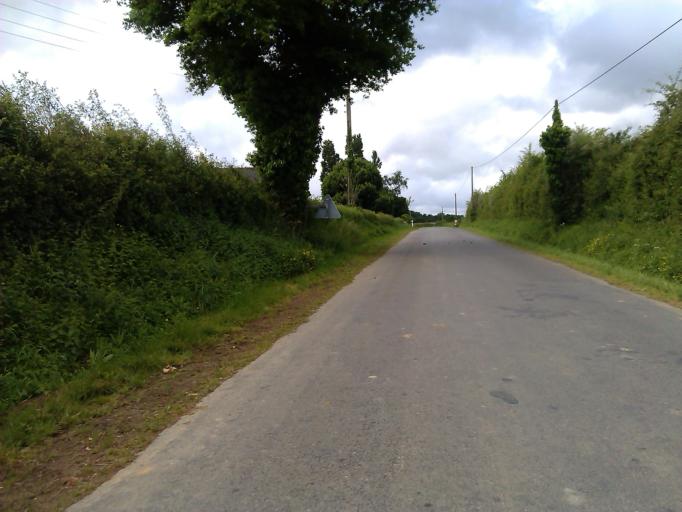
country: FR
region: Poitou-Charentes
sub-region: Departement de la Vienne
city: Availles-Limouzine
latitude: 46.1779
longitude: 0.6261
